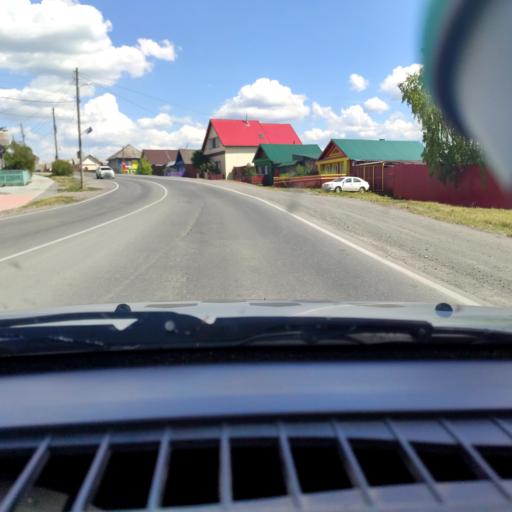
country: RU
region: Chelyabinsk
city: Satka
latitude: 55.0339
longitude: 59.0121
